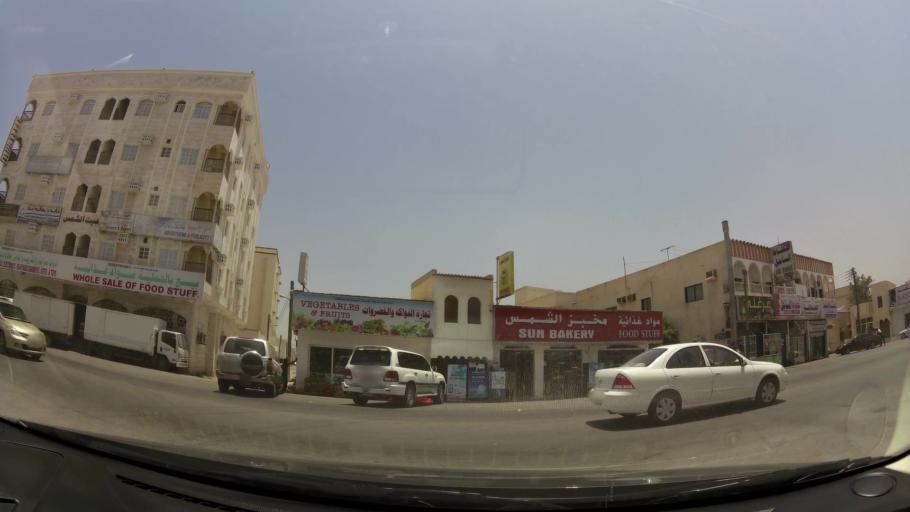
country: OM
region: Zufar
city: Salalah
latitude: 17.0170
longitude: 54.1065
